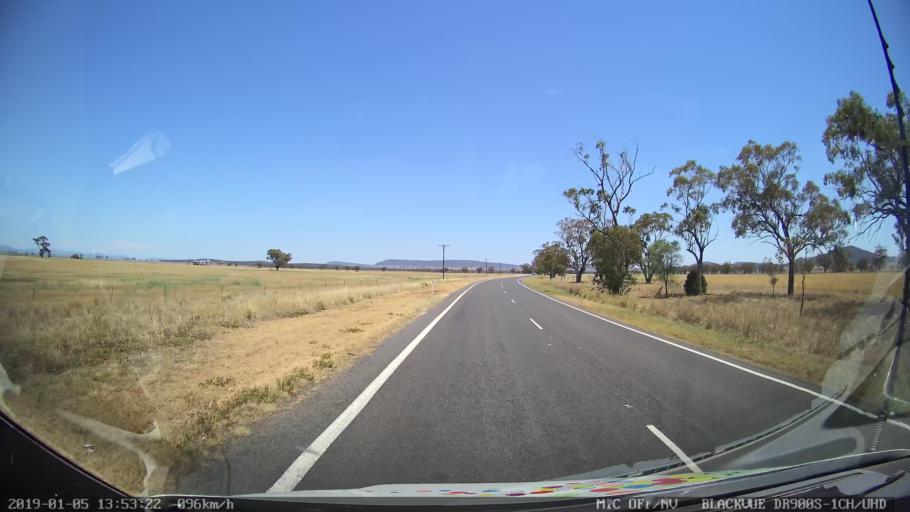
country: AU
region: New South Wales
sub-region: Gunnedah
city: Gunnedah
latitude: -31.0743
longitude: 150.2773
